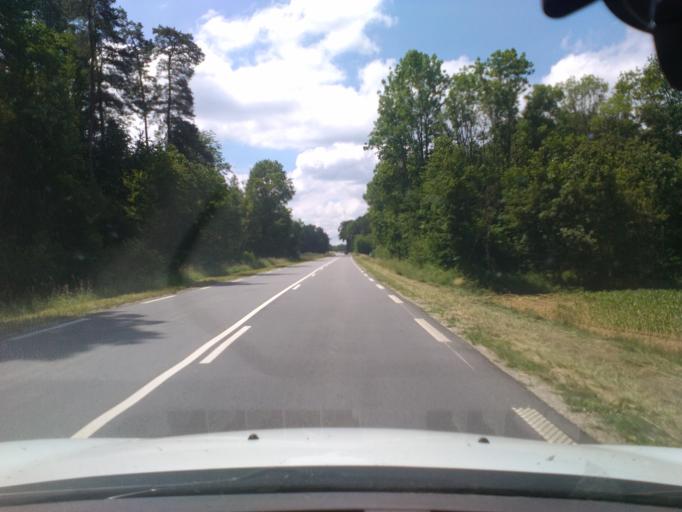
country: FR
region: Lorraine
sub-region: Departement des Vosges
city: Aydoilles
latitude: 48.2340
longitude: 6.5969
